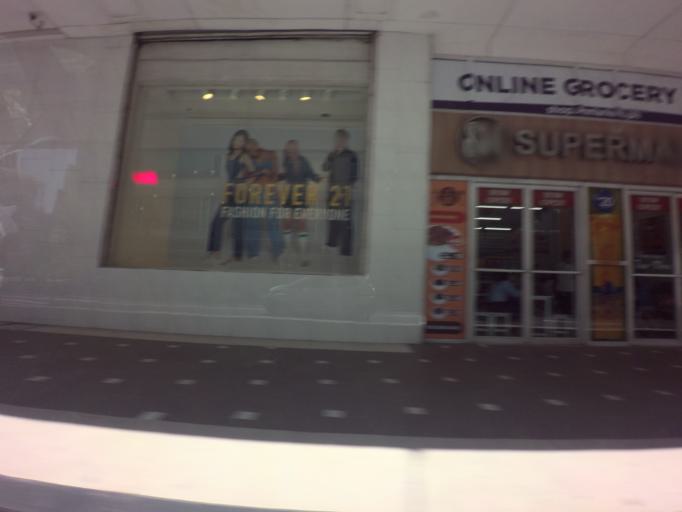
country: PH
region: Metro Manila
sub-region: Makati City
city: Makati City
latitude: 14.5504
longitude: 121.0261
